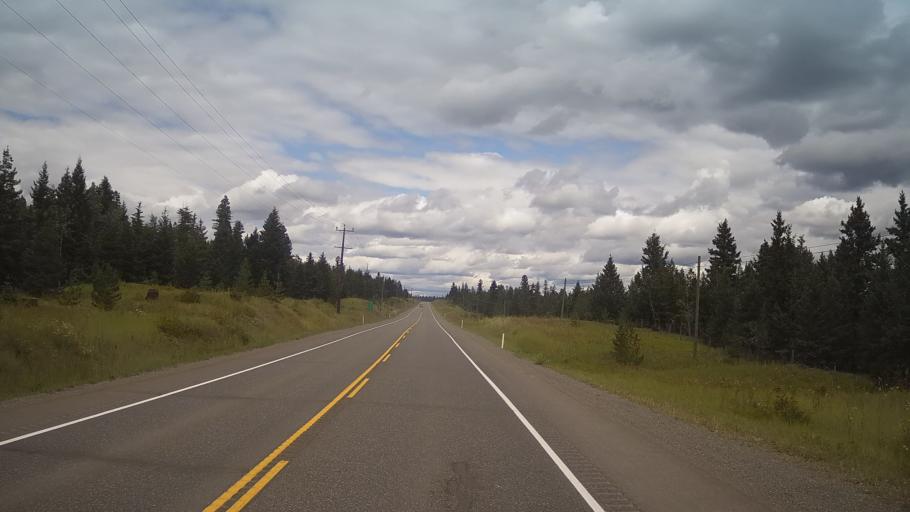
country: CA
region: British Columbia
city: Cache Creek
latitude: 51.1632
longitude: -121.5042
